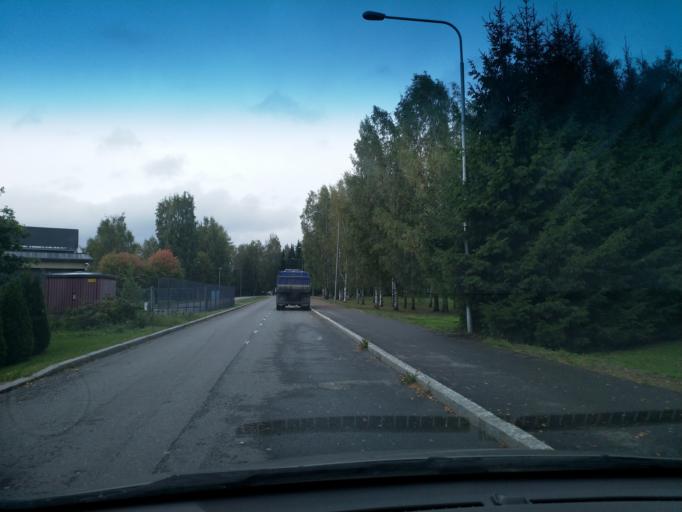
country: FI
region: Pirkanmaa
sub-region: Tampere
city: Tampere
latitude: 61.4747
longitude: 23.8419
